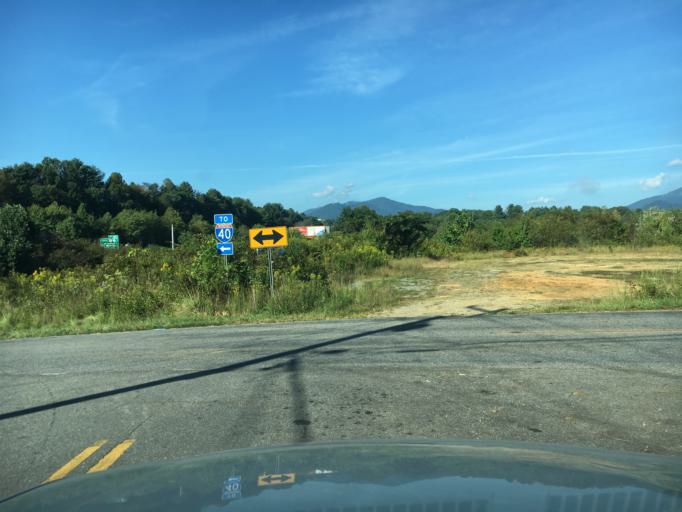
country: US
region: North Carolina
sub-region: Haywood County
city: Lake Junaluska
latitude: 35.5300
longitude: -82.9401
